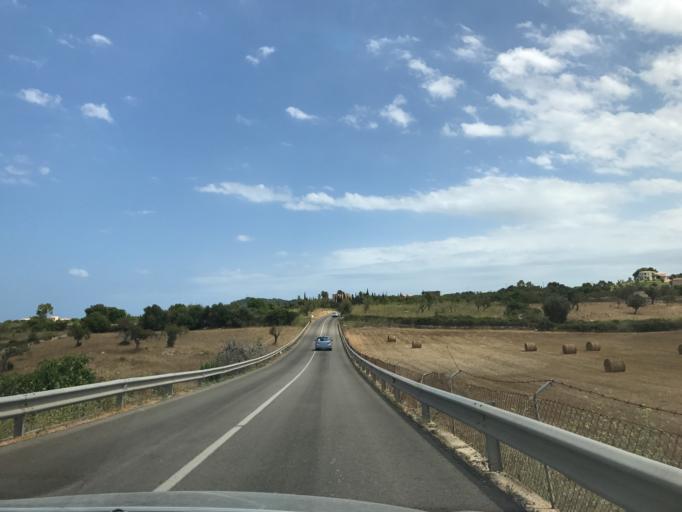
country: ES
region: Balearic Islands
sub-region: Illes Balears
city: Son Servera
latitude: 39.6426
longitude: 3.3479
